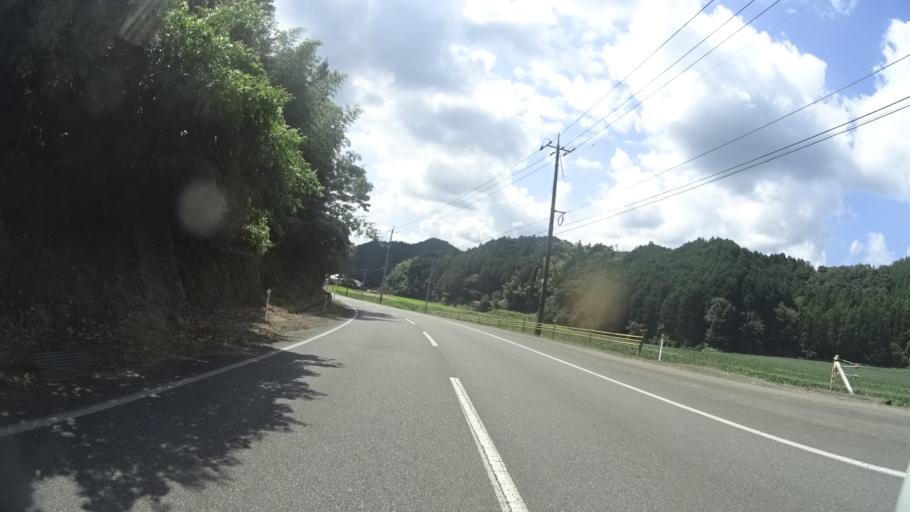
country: JP
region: Yamaguchi
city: Hagi
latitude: 34.4898
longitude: 131.5497
